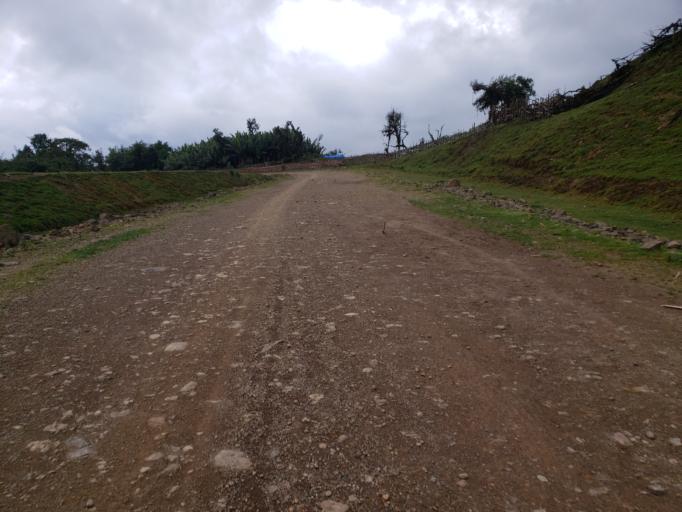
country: ET
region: Oromiya
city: Dodola
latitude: 6.6932
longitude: 39.3692
